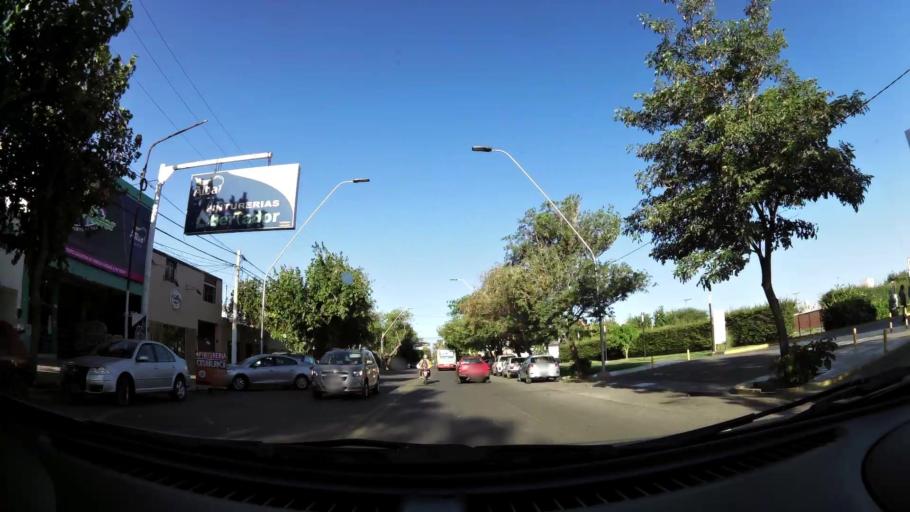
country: AR
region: San Juan
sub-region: Departamento de Santa Lucia
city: Santa Lucia
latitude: -31.5335
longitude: -68.5140
